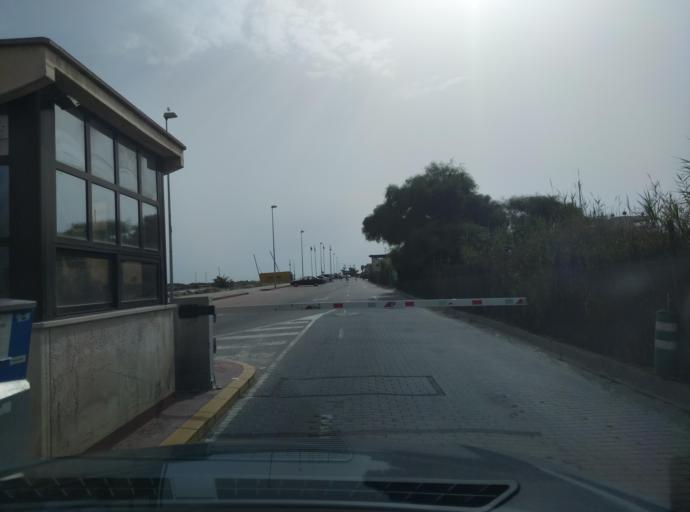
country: ES
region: Valencia
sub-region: Provincia de Alicante
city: Guardamar del Segura
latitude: 38.1095
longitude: -0.6487
